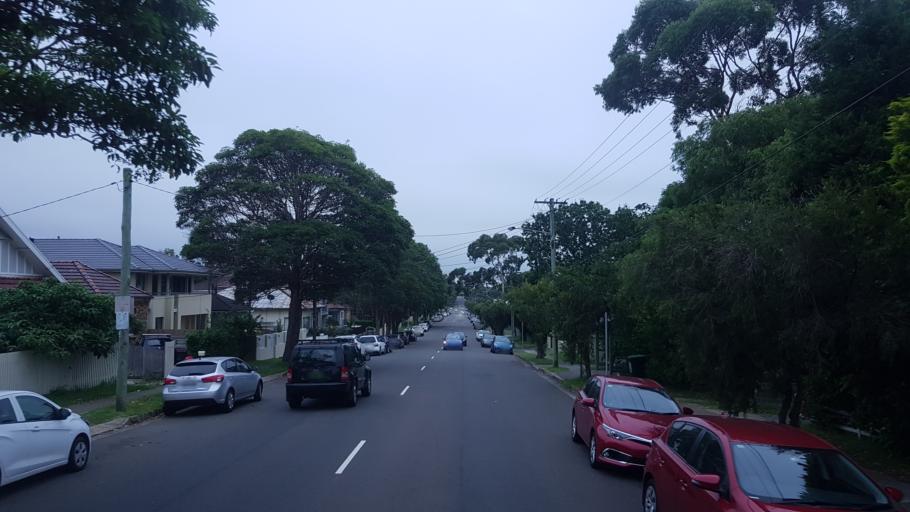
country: AU
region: New South Wales
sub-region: Warringah
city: Narraweena
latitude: -33.7547
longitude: 151.2738
